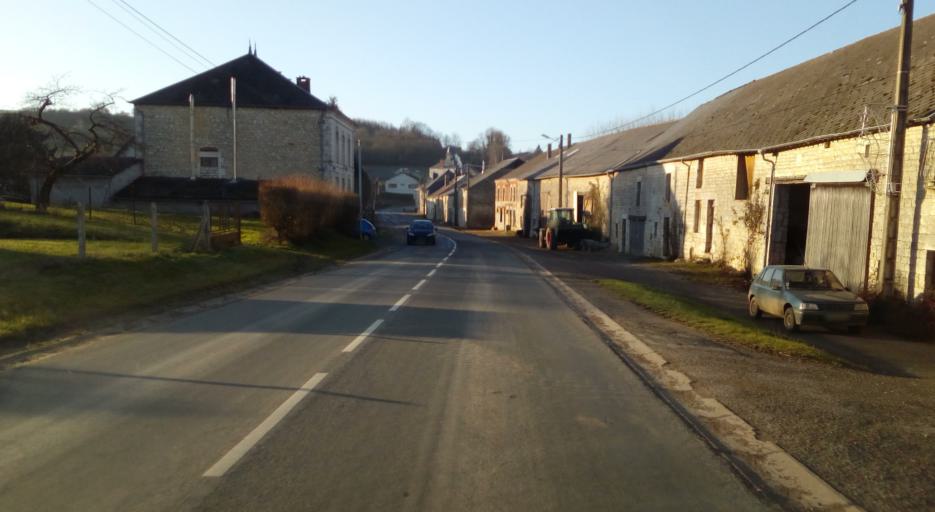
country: FR
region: Champagne-Ardenne
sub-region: Departement des Ardennes
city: Rimogne
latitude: 49.7772
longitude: 4.4004
